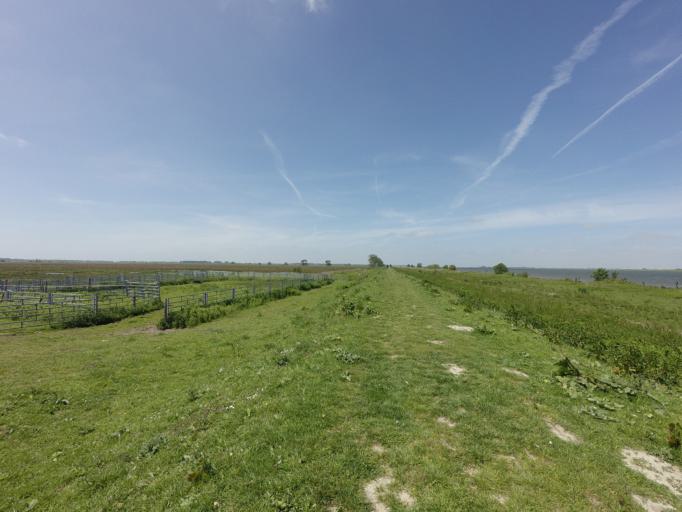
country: NL
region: South Holland
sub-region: Gemeente Spijkenisse
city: Spijkenisse
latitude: 51.7498
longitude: 4.2921
